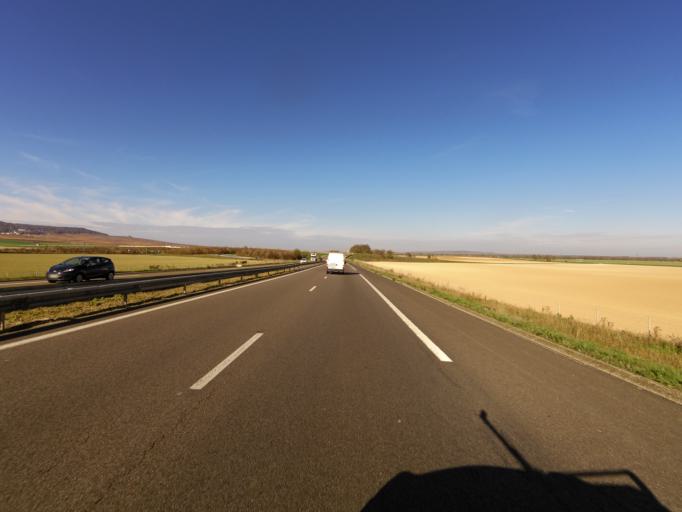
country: FR
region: Champagne-Ardenne
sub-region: Departement de la Marne
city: Verzy
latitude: 49.1468
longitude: 4.2097
